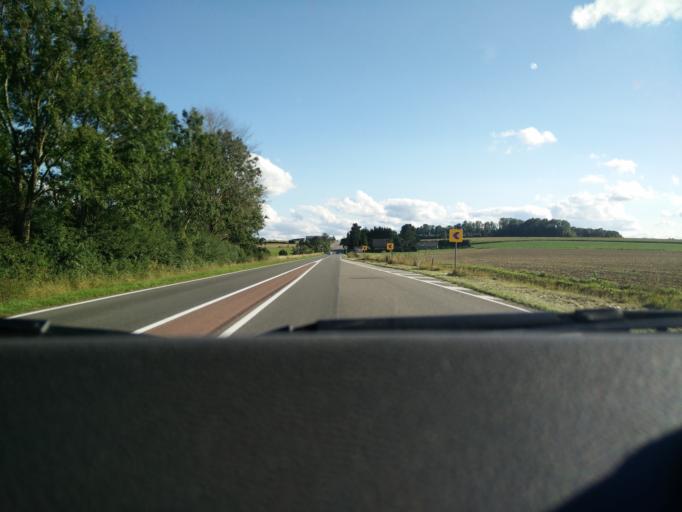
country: BE
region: Wallonia
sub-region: Province du Hainaut
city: Beaumont
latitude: 50.2094
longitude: 4.2256
